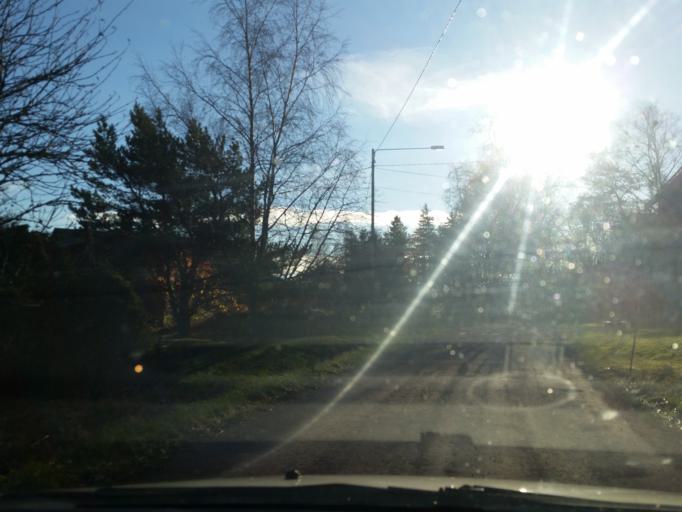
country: AX
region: Alands skaergard
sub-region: Braendoe
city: Braendoe
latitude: 60.4609
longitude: 21.0715
